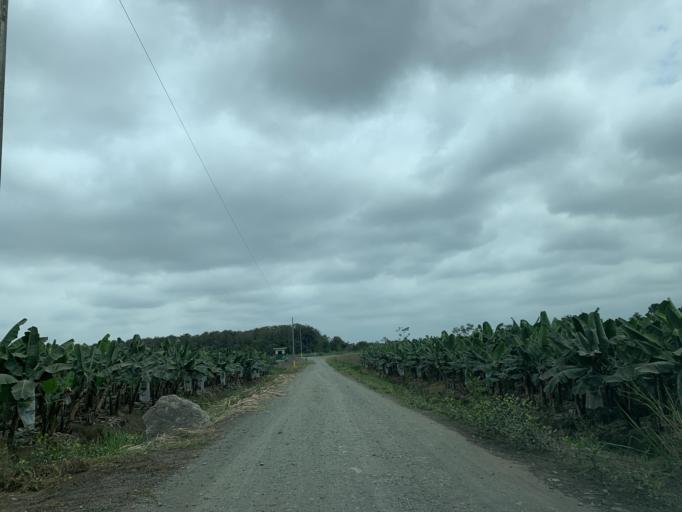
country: EC
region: Guayas
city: Coronel Marcelino Mariduena
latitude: -2.3310
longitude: -79.4544
